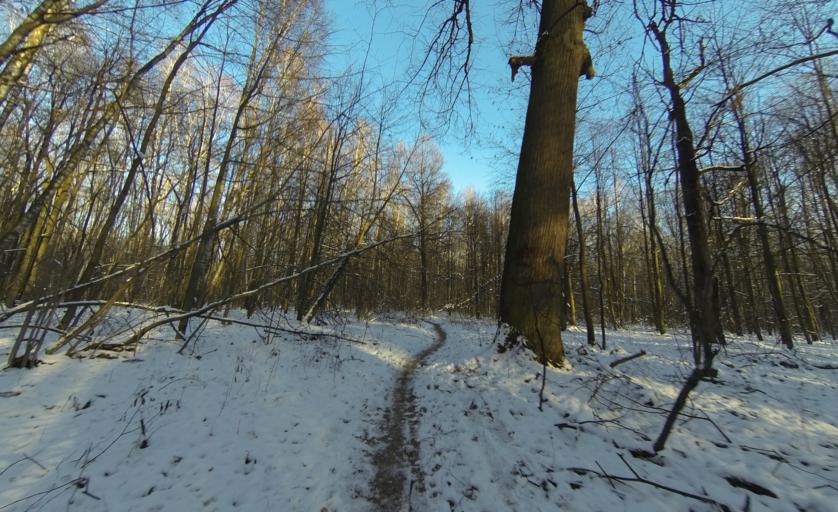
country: RU
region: Moskovskaya
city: Bogorodskoye
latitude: 55.8345
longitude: 37.6988
